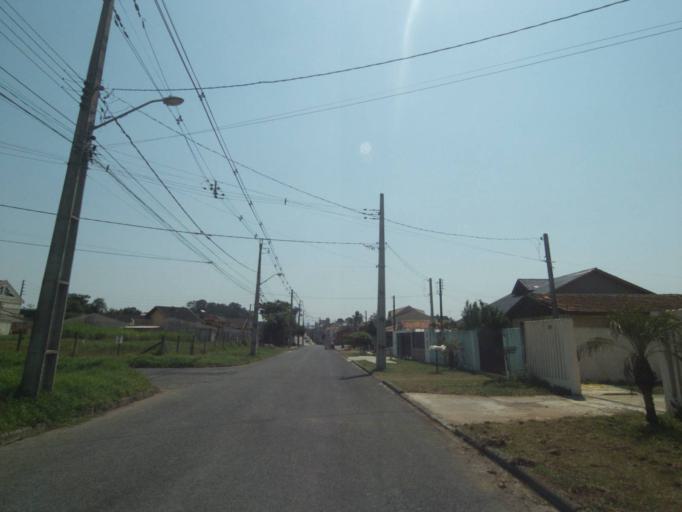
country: BR
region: Parana
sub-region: Sao Jose Dos Pinhais
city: Sao Jose dos Pinhais
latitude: -25.5025
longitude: -49.2706
